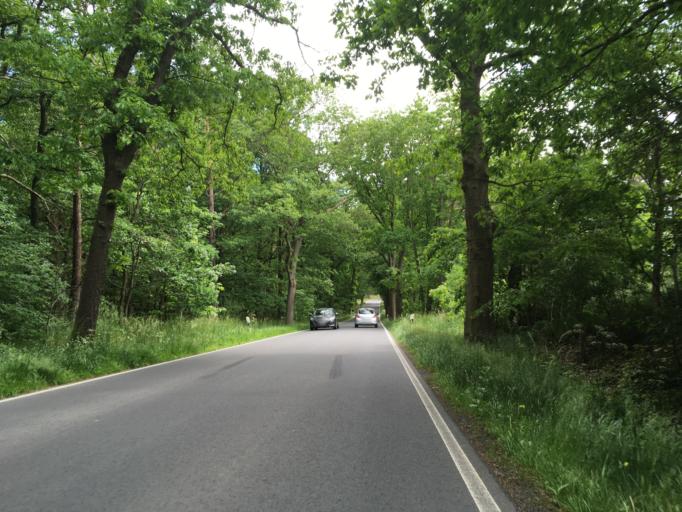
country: DE
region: Brandenburg
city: Falkenberg
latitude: 52.7654
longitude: 13.9650
